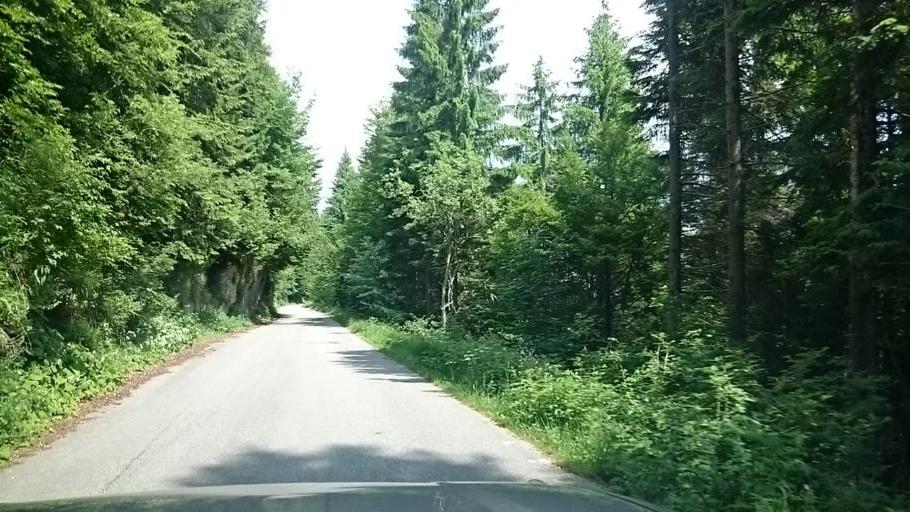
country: IT
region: Veneto
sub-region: Provincia di Vicenza
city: Foza
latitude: 45.9157
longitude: 11.6473
